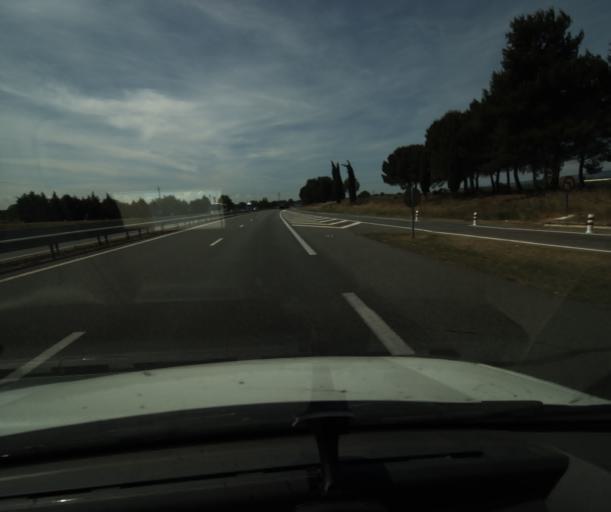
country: FR
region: Languedoc-Roussillon
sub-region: Departement de l'Aude
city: Bram
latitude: 43.2295
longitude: 2.1134
